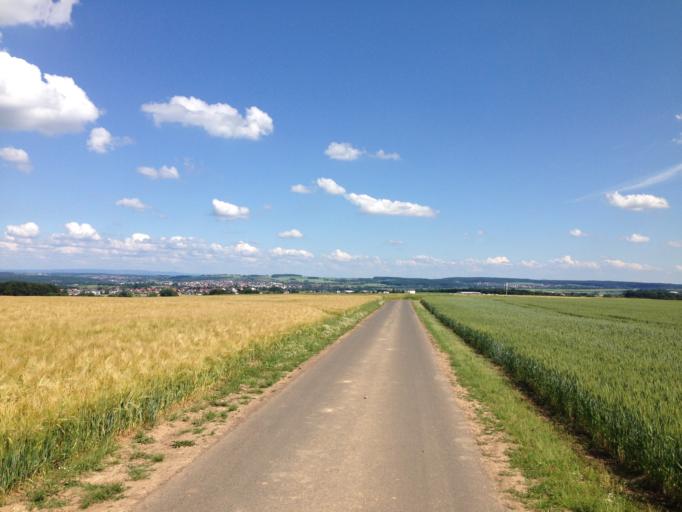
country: DE
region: Hesse
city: Allendorf an der Lahn
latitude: 50.5371
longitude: 8.5887
